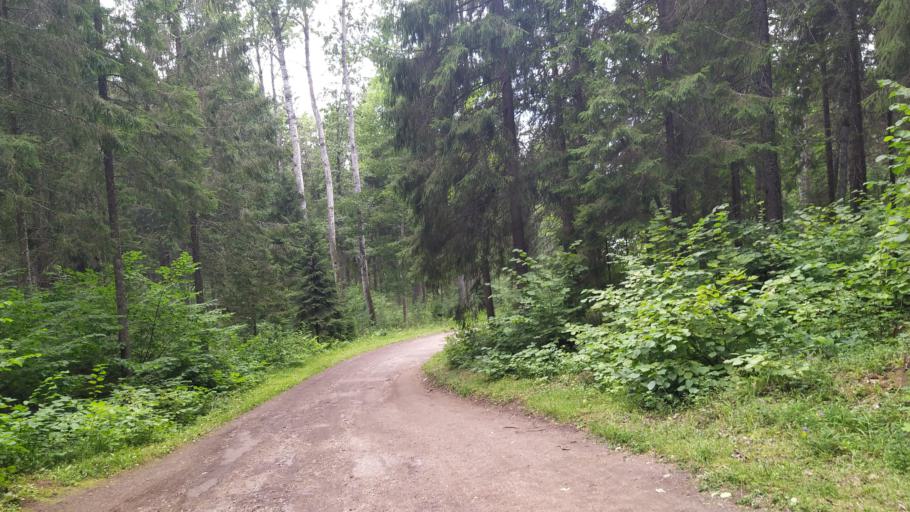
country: RU
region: Pskov
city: Pushkinskiye Gory
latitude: 57.0588
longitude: 28.9378
